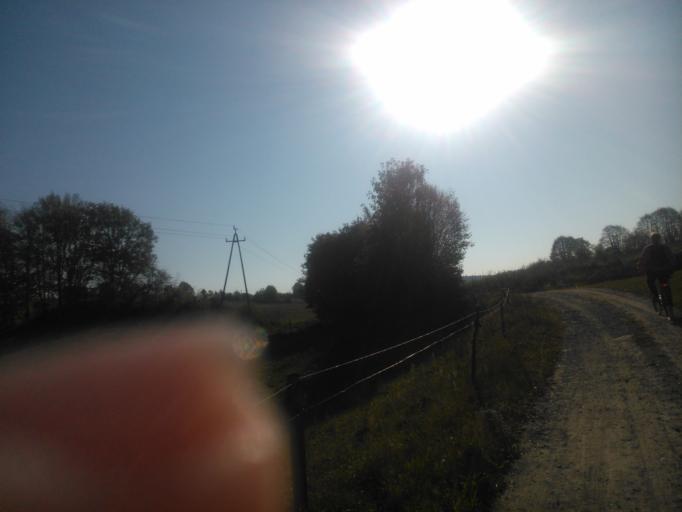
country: PL
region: Kujawsko-Pomorskie
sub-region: Powiat brodnicki
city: Gorzno
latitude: 53.2134
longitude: 19.6602
